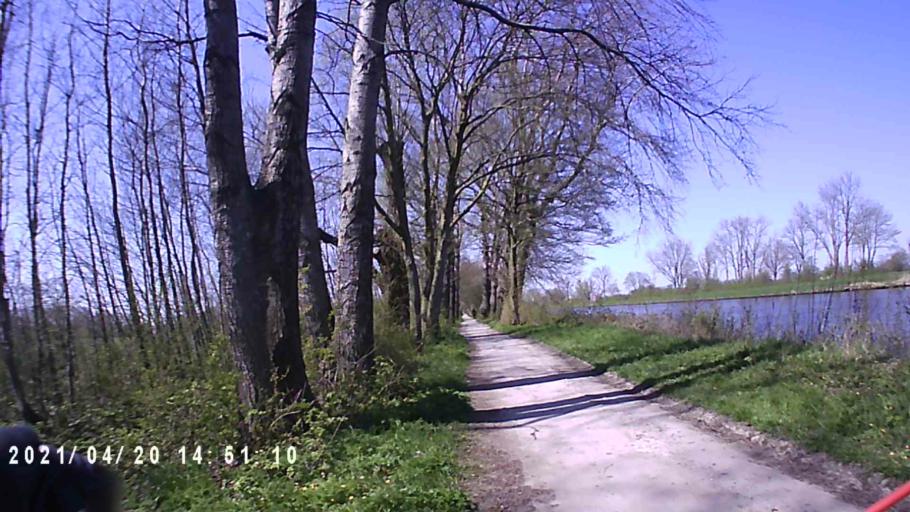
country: NL
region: Groningen
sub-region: Gemeente Groningen
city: Korrewegwijk
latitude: 53.2465
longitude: 6.5422
